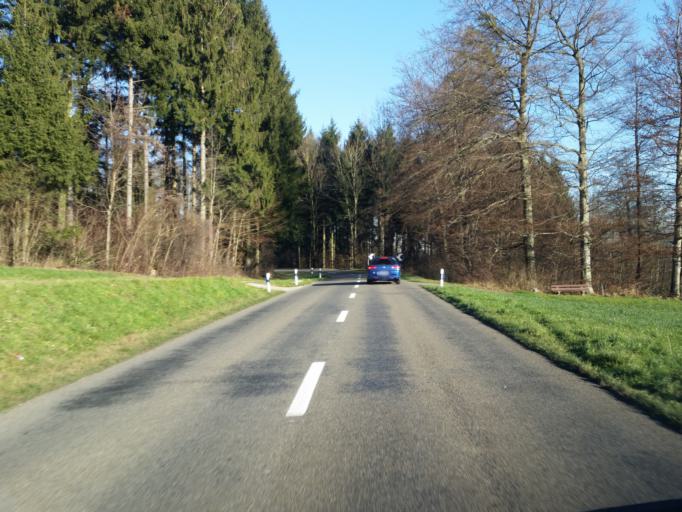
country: CH
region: Aargau
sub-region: Bezirk Bremgarten
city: Rudolfstetten
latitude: 47.3744
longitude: 8.3765
